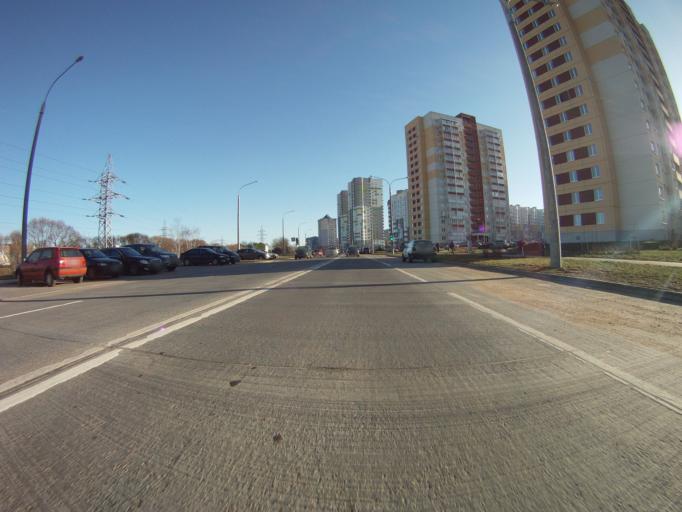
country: BY
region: Minsk
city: Novoye Medvezhino
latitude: 53.8755
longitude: 27.4720
